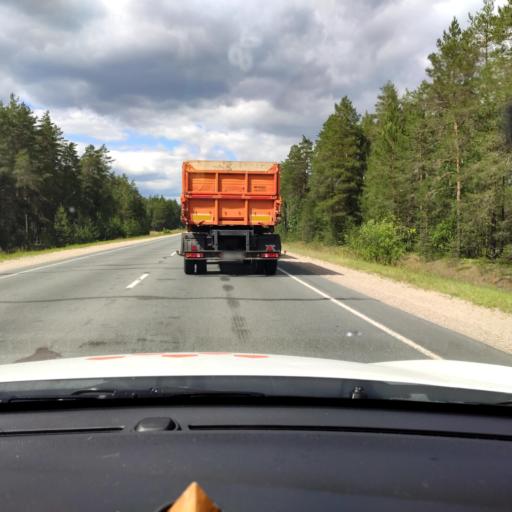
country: RU
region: Mariy-El
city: Krasnogorskiy
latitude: 56.0875
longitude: 48.3514
